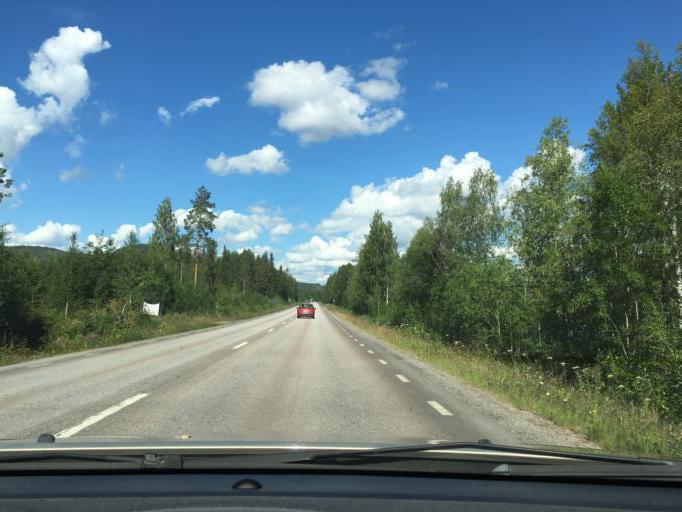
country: SE
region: Norrbotten
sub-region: Overkalix Kommun
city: OEverkalix
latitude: 66.2980
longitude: 22.8151
